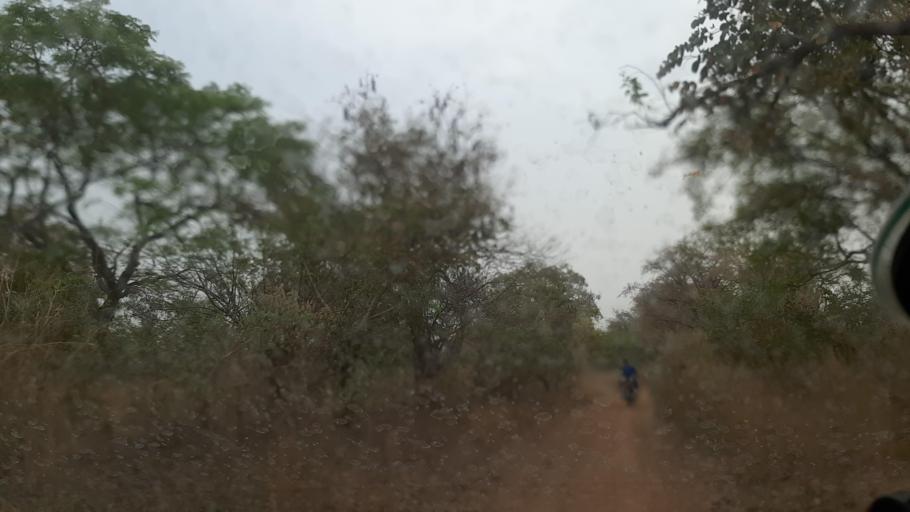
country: BF
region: Boucle du Mouhoun
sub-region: Province des Banwa
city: Salanso
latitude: 11.8537
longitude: -4.4289
